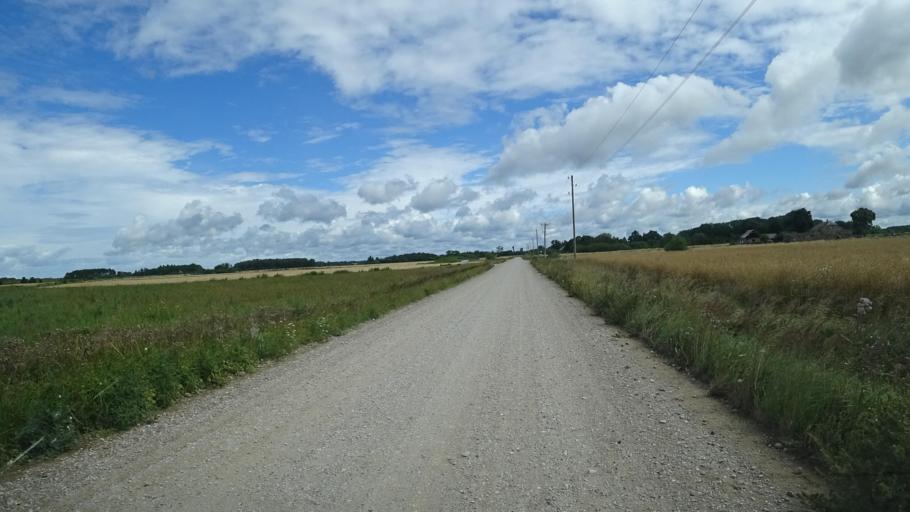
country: LV
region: Liepaja
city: Vec-Liepaja
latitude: 56.6524
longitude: 21.0521
